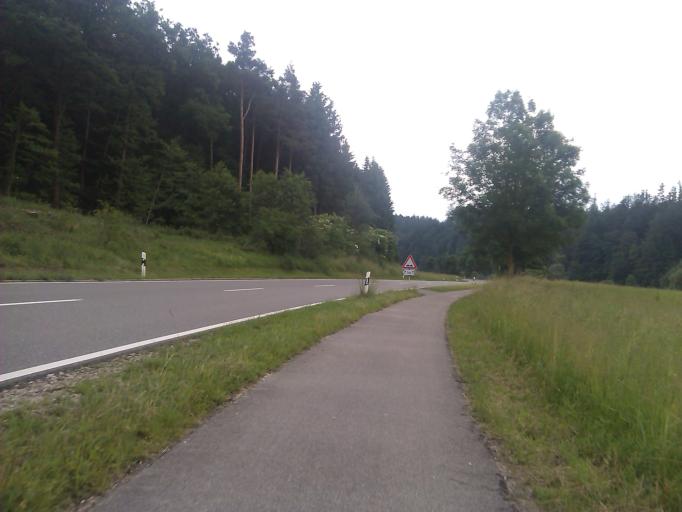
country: DE
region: Baden-Wuerttemberg
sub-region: Regierungsbezirk Stuttgart
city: Abtsgmund
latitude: 48.9053
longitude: 9.9754
